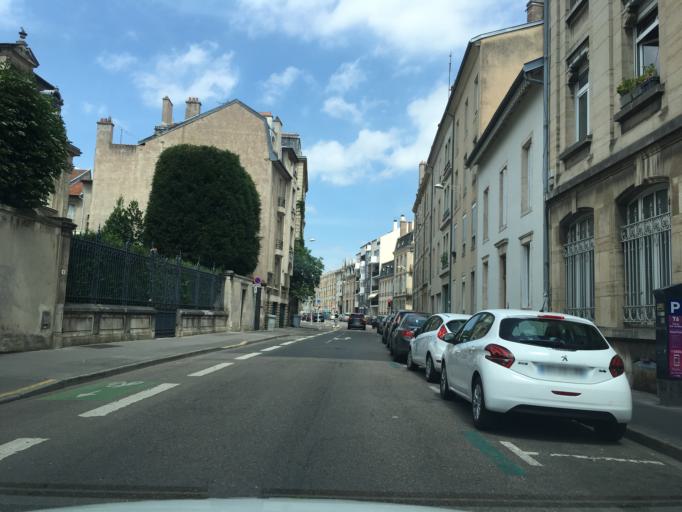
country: FR
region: Lorraine
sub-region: Departement de Meurthe-et-Moselle
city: Nancy
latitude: 48.6905
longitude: 6.1913
